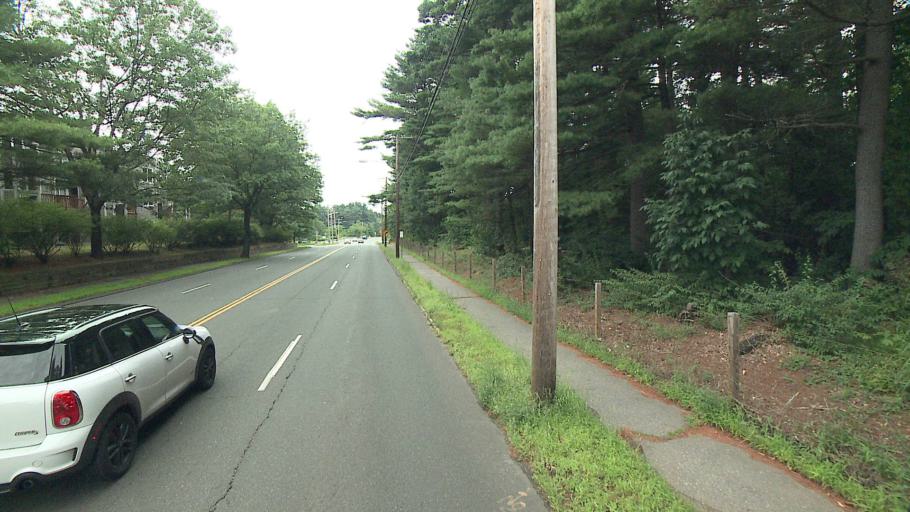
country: US
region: Connecticut
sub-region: New Haven County
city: New Haven
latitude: 41.3522
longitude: -72.9131
